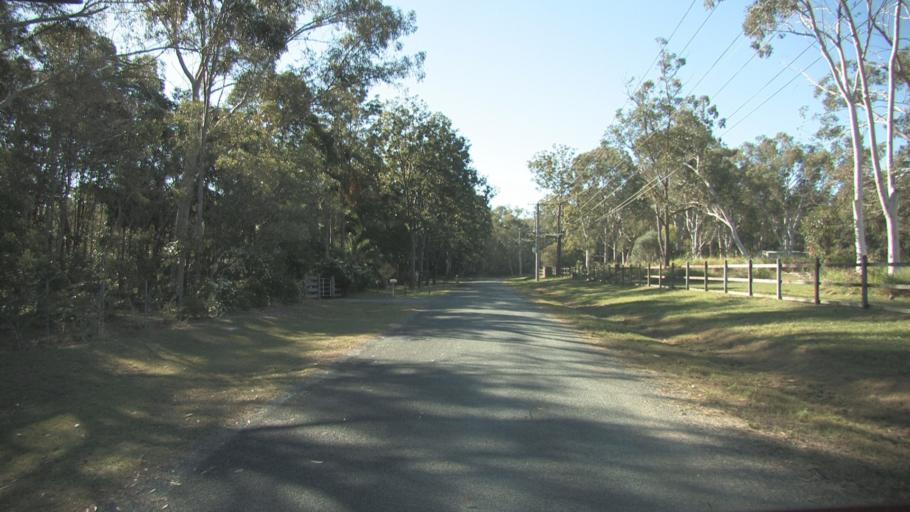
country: AU
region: Queensland
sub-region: Logan
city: Logan Reserve
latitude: -27.7298
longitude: 153.0833
